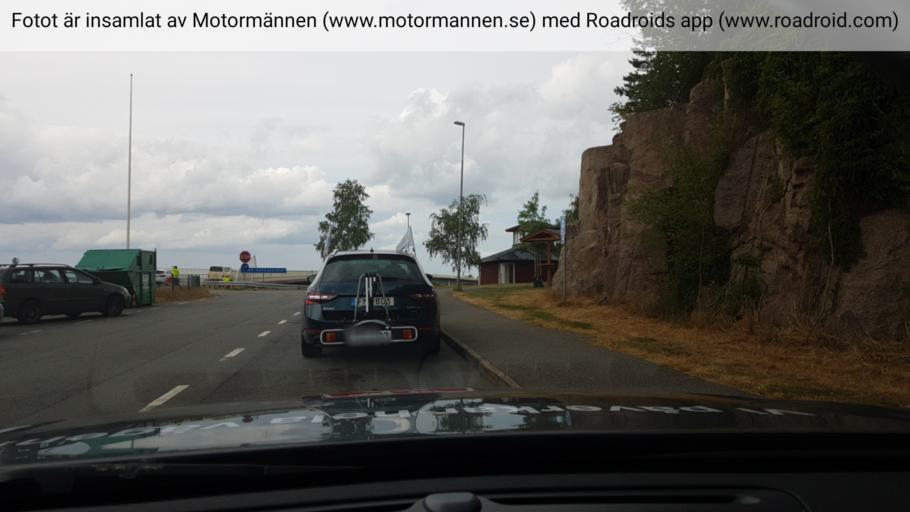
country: SE
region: OErebro
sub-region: Askersunds Kommun
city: Askersund
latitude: 58.8106
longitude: 14.9385
